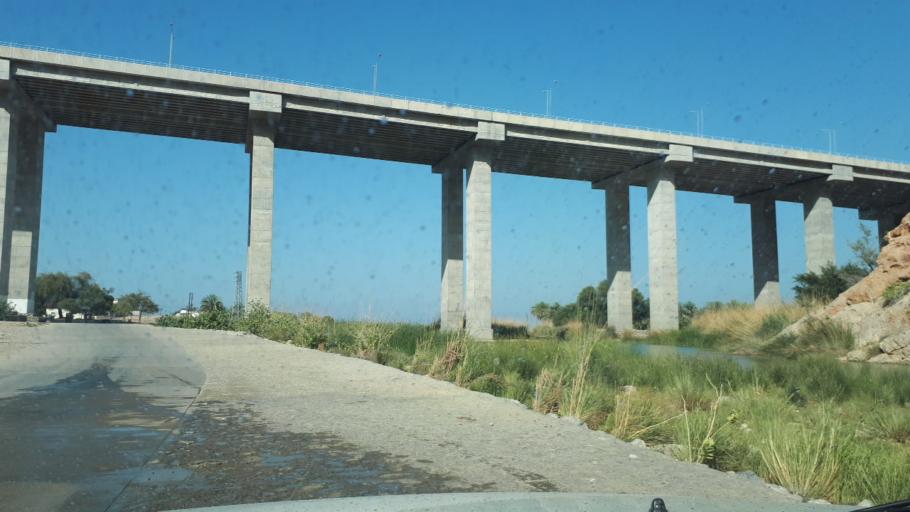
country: OM
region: Ash Sharqiyah
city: Sur
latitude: 22.8240
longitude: 59.2598
